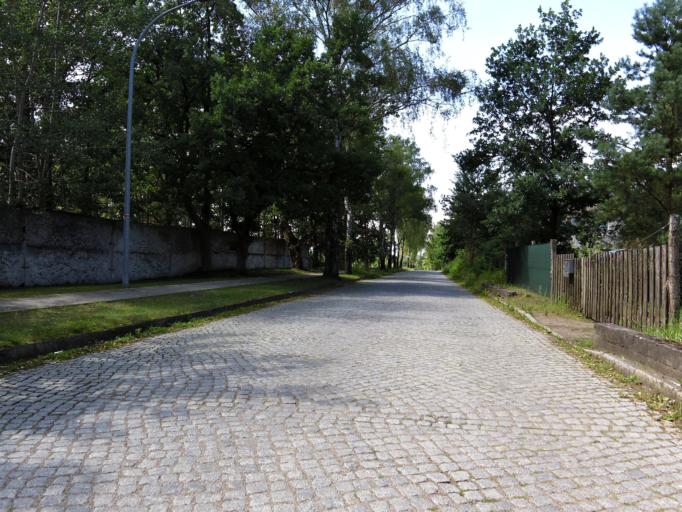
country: DE
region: Brandenburg
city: Furstenberg
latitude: 53.1944
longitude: 13.1541
